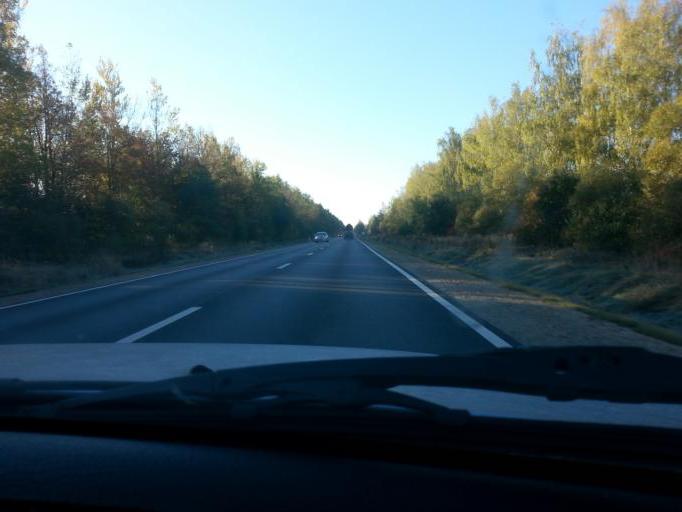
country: LV
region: Jelgava
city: Jelgava
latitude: 56.5127
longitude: 23.7023
